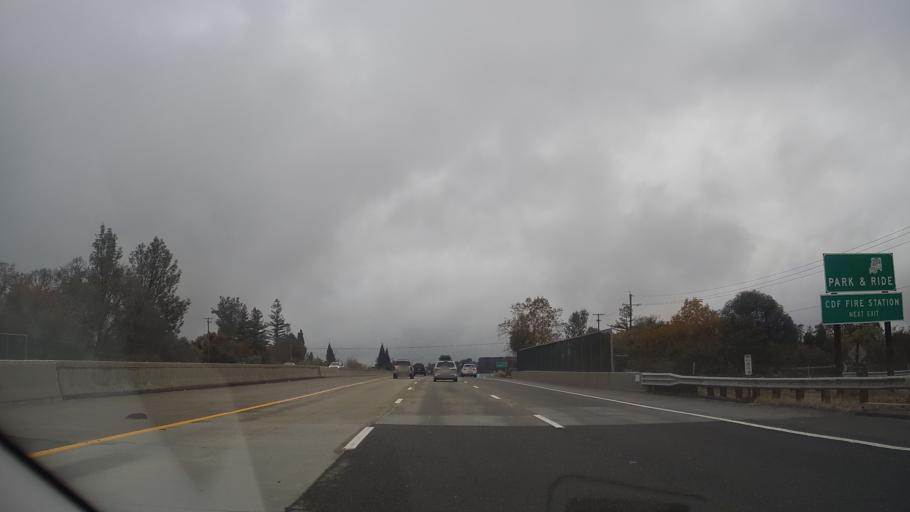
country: US
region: California
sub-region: Placer County
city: North Auburn
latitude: 38.9398
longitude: -121.0516
